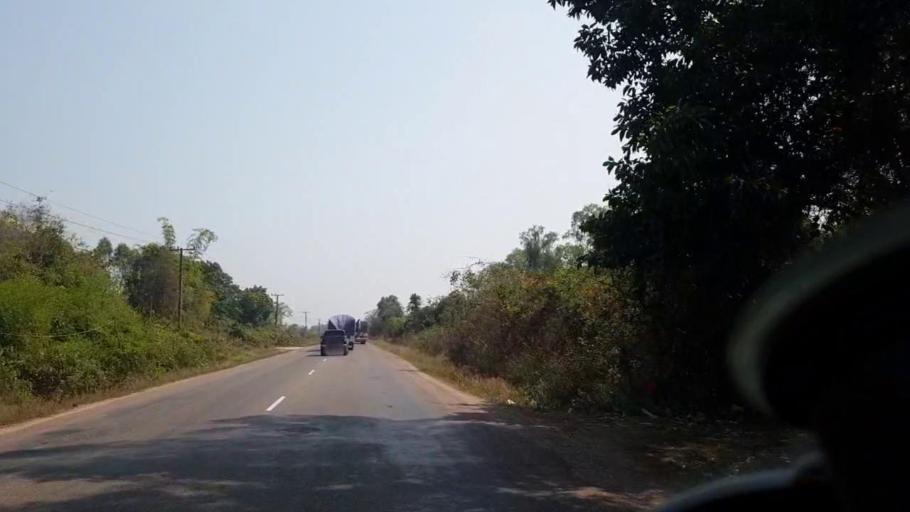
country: TH
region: Nong Khai
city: Phon Phisai
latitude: 18.0890
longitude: 103.0074
